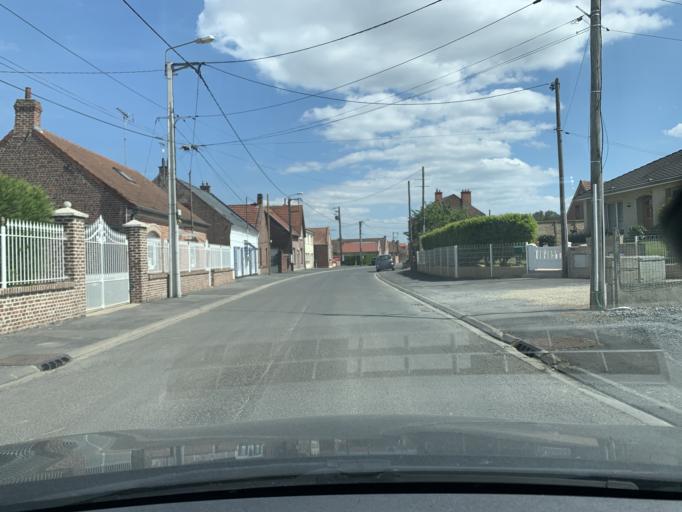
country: FR
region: Nord-Pas-de-Calais
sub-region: Departement du Nord
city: Aubigny-au-Bac
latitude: 50.2307
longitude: 3.1690
